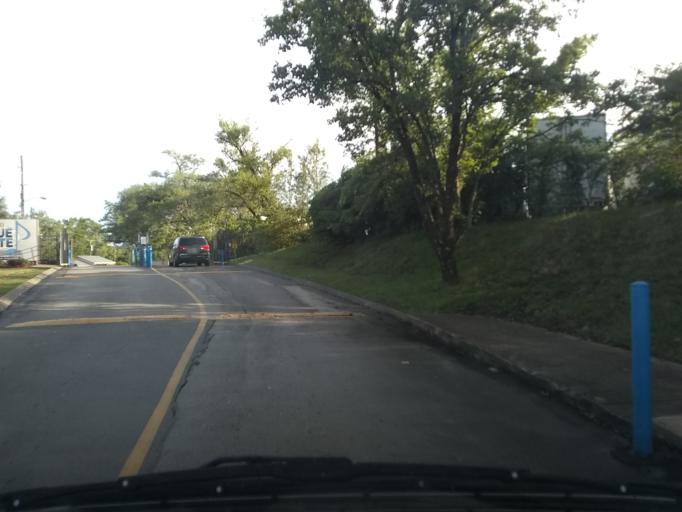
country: US
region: Tennessee
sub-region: Davidson County
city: Nashville
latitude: 36.1316
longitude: -86.7140
